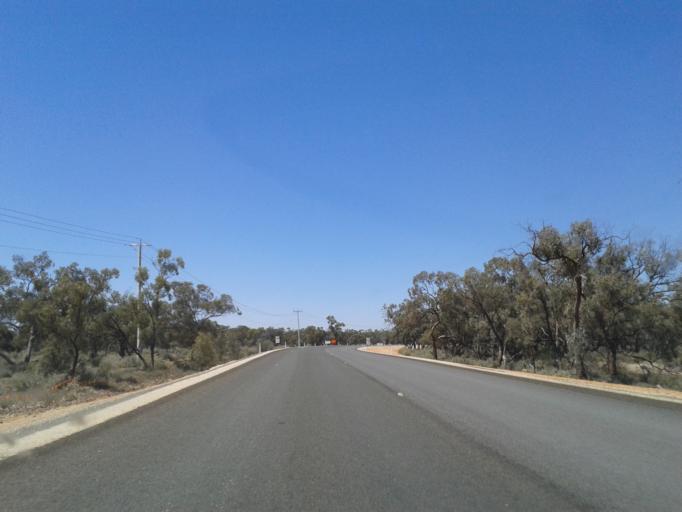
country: AU
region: New South Wales
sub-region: Wentworth
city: Gol Gol
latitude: -34.5585
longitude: 142.7191
